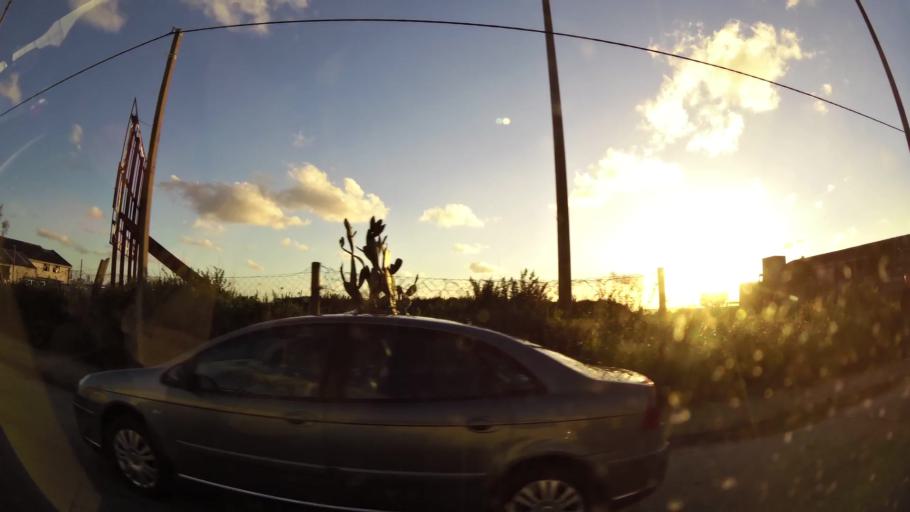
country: UY
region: Montevideo
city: Montevideo
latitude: -34.8765
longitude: -56.2090
